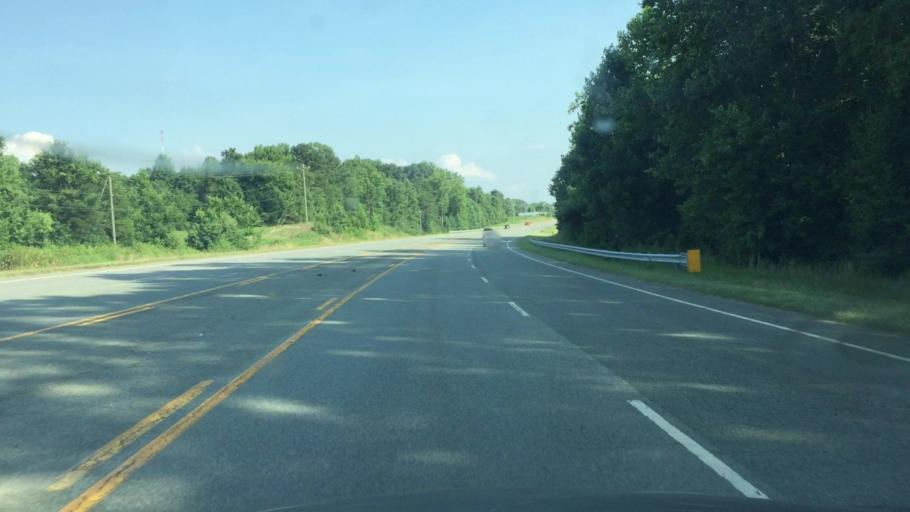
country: US
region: North Carolina
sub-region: Rockingham County
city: Reidsville
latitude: 36.3211
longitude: -79.6345
